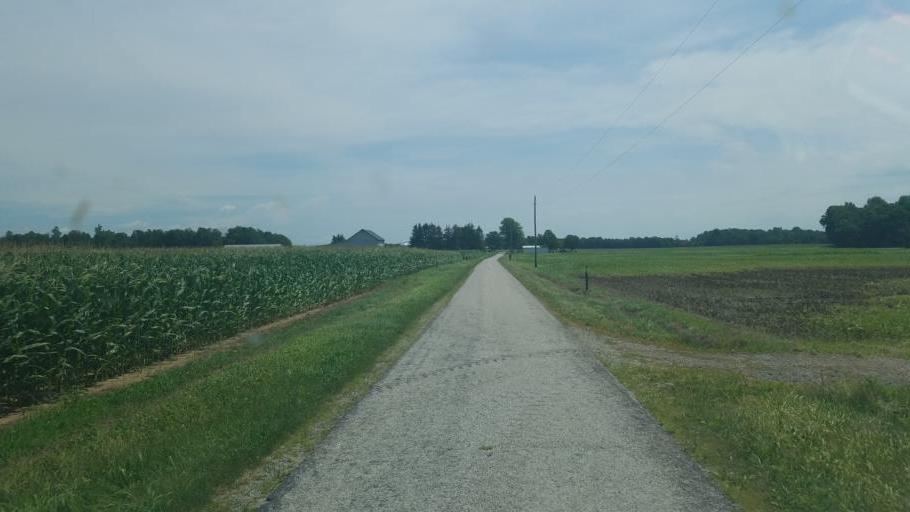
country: US
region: Ohio
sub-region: Crawford County
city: Bucyrus
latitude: 40.8739
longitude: -82.9564
